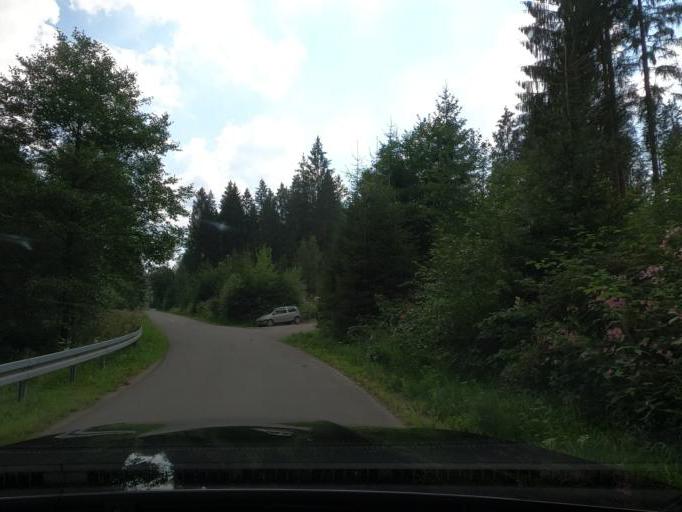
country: DE
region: Lower Saxony
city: Clausthal-Zellerfeld
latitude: 51.7837
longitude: 10.2996
